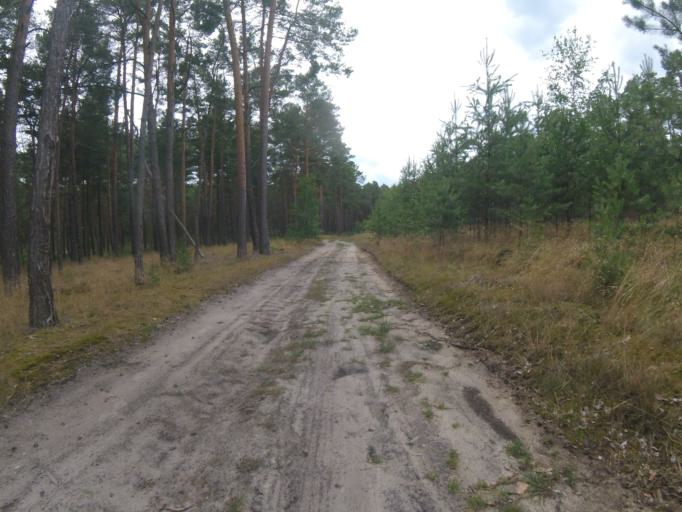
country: DE
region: Brandenburg
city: Bestensee
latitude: 52.2621
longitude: 13.7046
